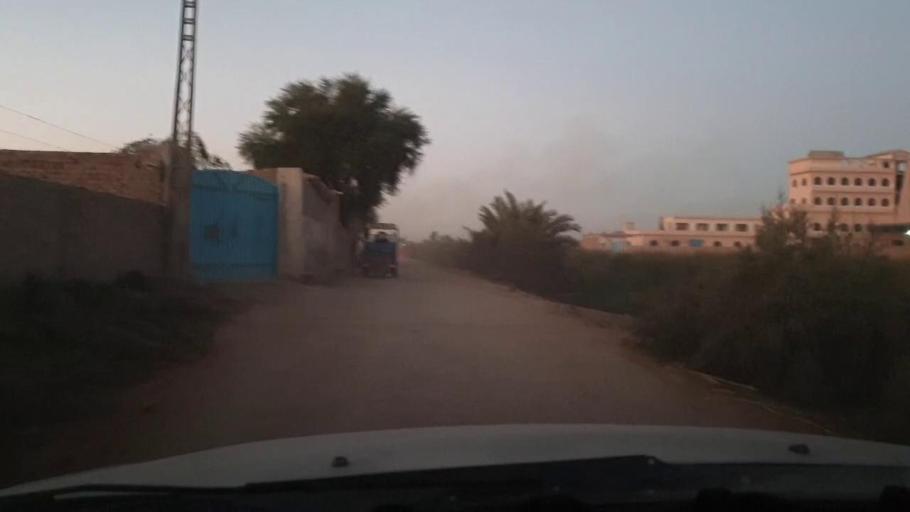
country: PK
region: Sindh
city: Ghotki
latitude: 27.9840
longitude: 69.2870
